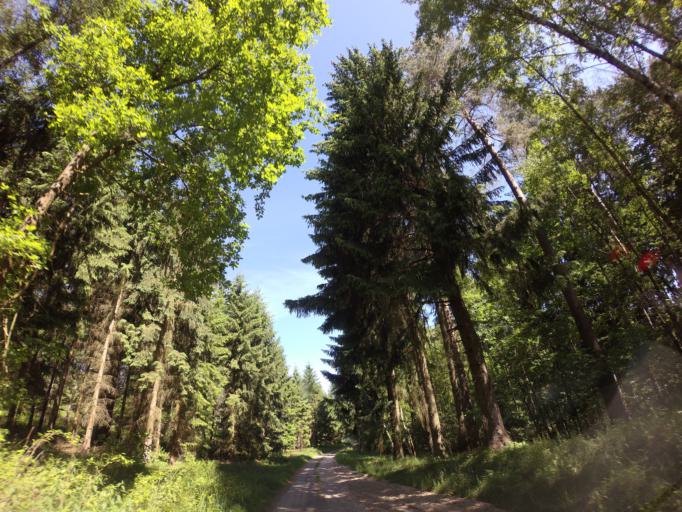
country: PL
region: West Pomeranian Voivodeship
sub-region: Powiat choszczenski
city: Recz
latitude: 53.3107
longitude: 15.6021
